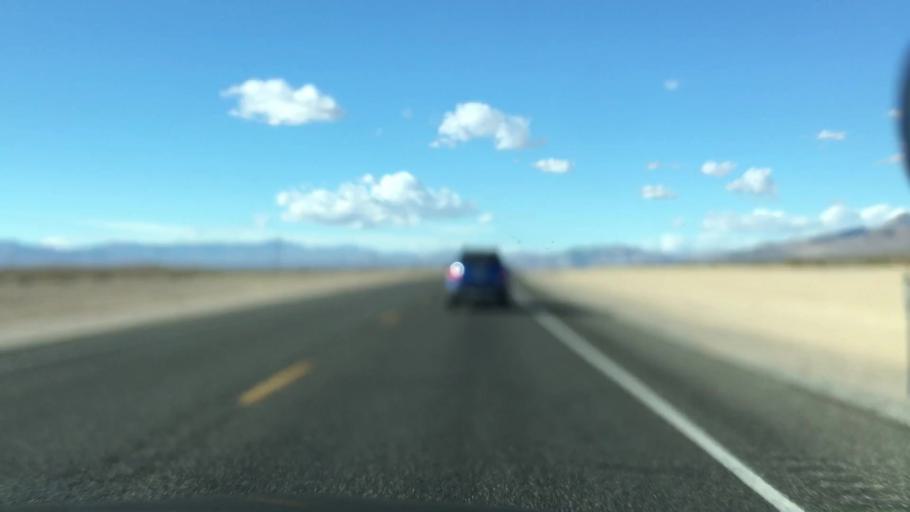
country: US
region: Nevada
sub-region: Nye County
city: Beatty
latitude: 36.7289
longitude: -116.6298
